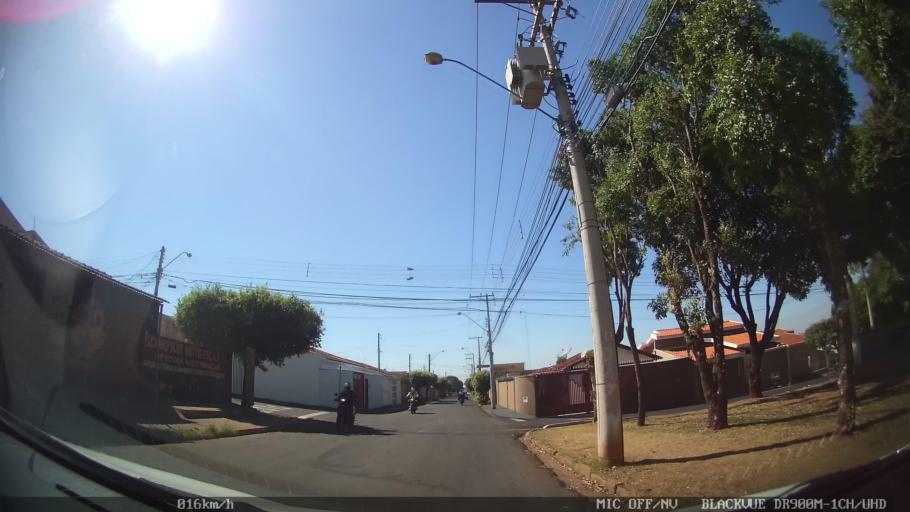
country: BR
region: Sao Paulo
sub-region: Sao Jose Do Rio Preto
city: Sao Jose do Rio Preto
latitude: -20.7702
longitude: -49.4096
